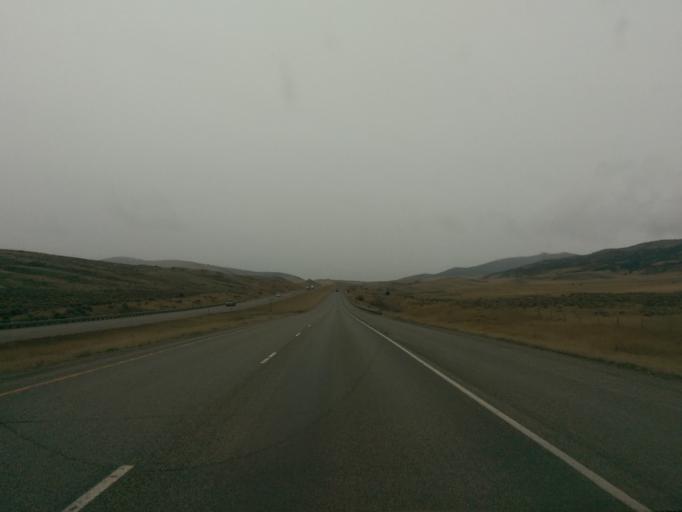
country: US
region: Montana
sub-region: Gallatin County
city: Three Forks
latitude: 45.9082
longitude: -111.7940
